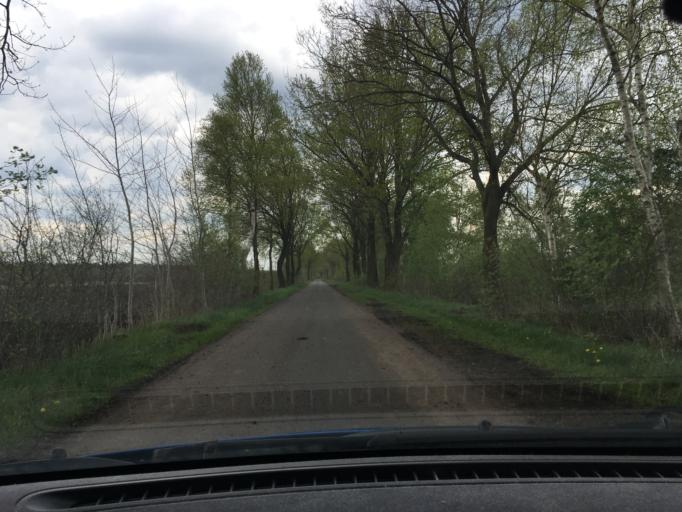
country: DE
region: Lower Saxony
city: Radbruch
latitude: 53.2948
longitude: 10.2667
